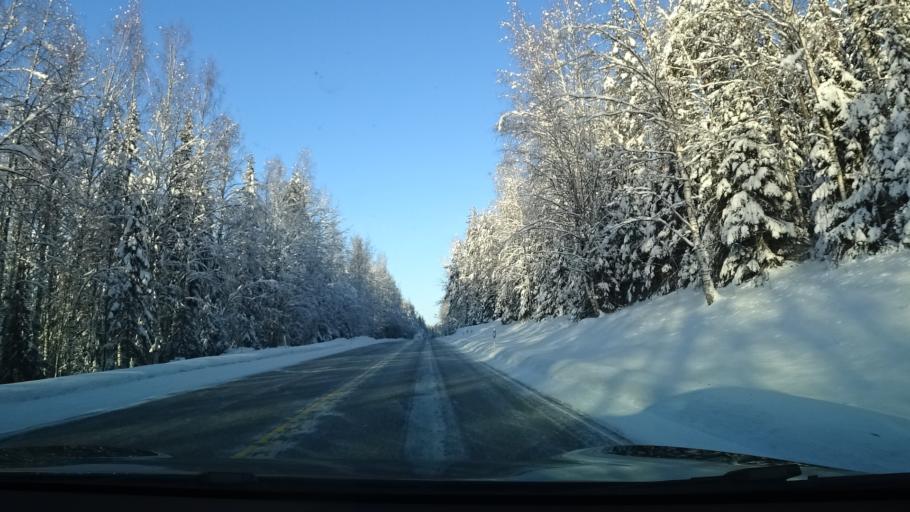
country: FI
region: Northern Savo
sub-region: Varkaus
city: Kangaslampi
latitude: 62.4672
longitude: 28.3235
